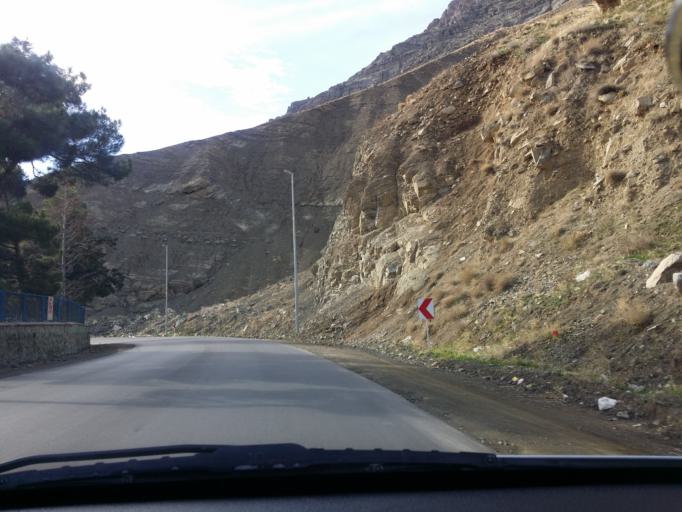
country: IR
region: Alborz
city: Karaj
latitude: 35.9698
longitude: 51.0937
